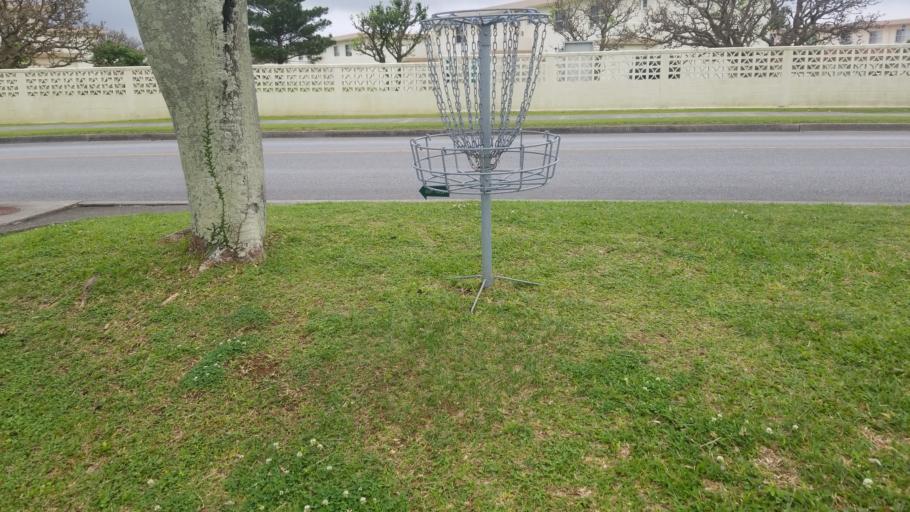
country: JP
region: Okinawa
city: Okinawa
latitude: 26.3365
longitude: 127.7751
